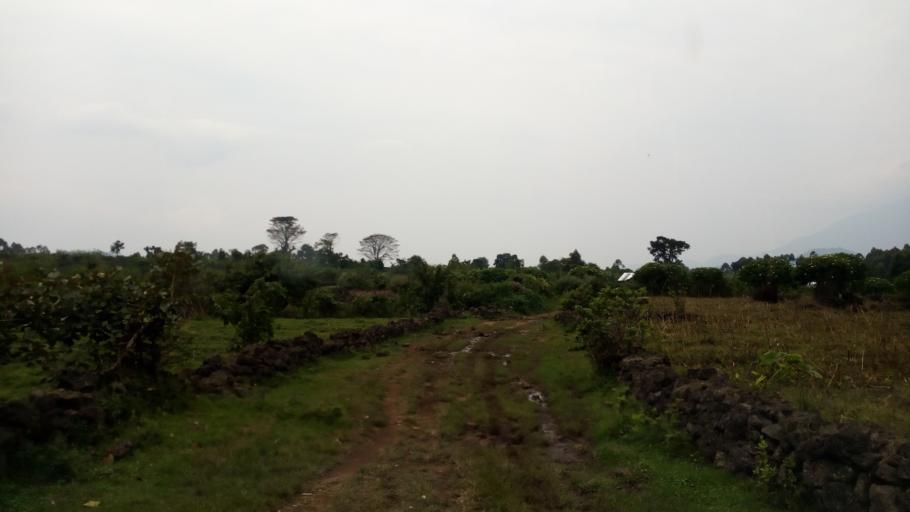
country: UG
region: Western Region
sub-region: Kisoro District
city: Kisoro
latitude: -1.2651
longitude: 29.6072
